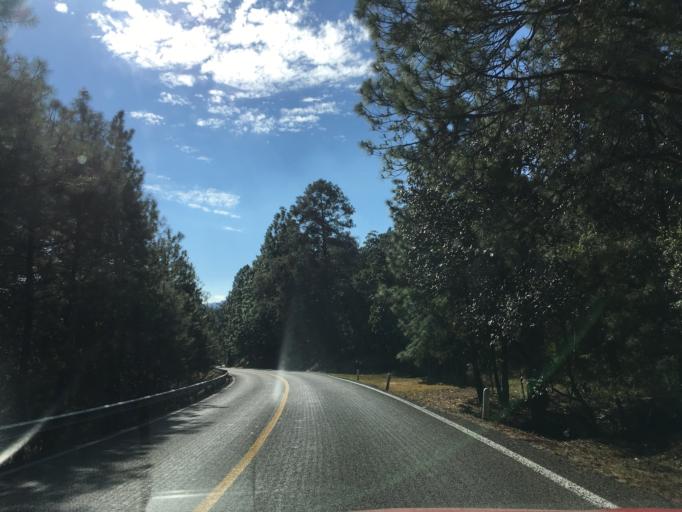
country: MX
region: Michoacan
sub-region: Hidalgo
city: Tierras Coloradas (San Pedro)
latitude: 19.6712
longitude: -100.7222
